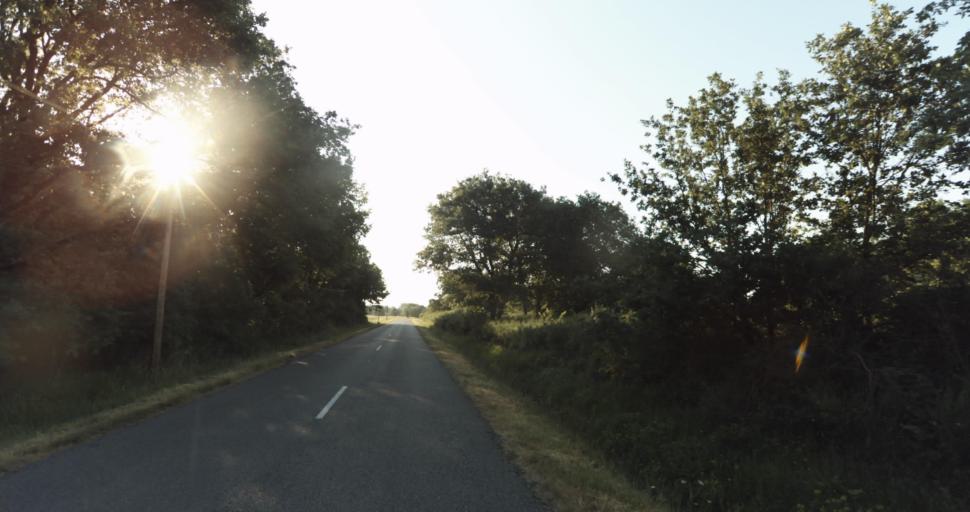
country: FR
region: Midi-Pyrenees
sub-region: Departement de la Haute-Garonne
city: Fontenilles
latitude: 43.5455
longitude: 1.2081
